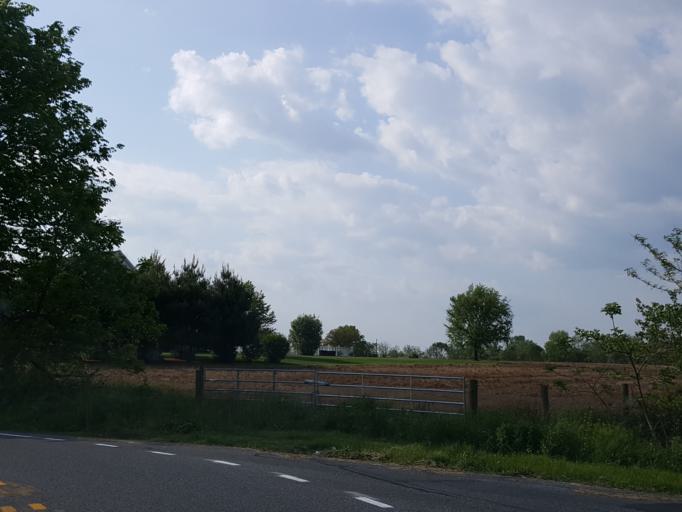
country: US
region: Pennsylvania
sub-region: Lebanon County
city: Campbelltown
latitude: 40.2586
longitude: -76.6087
